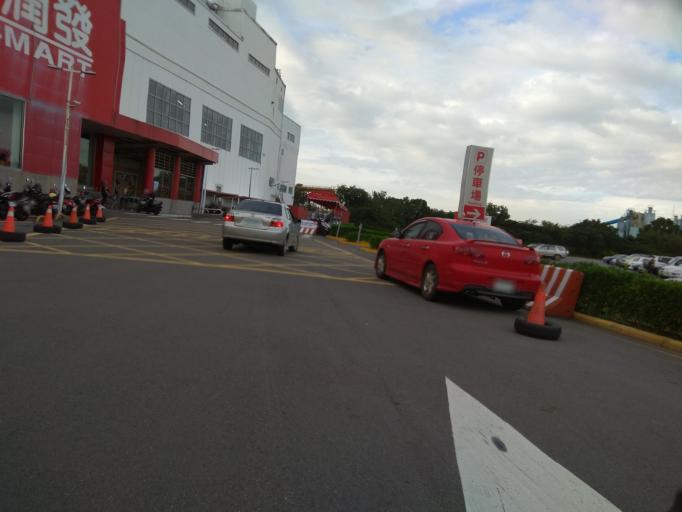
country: TW
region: Taiwan
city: Daxi
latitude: 24.9209
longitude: 121.2138
